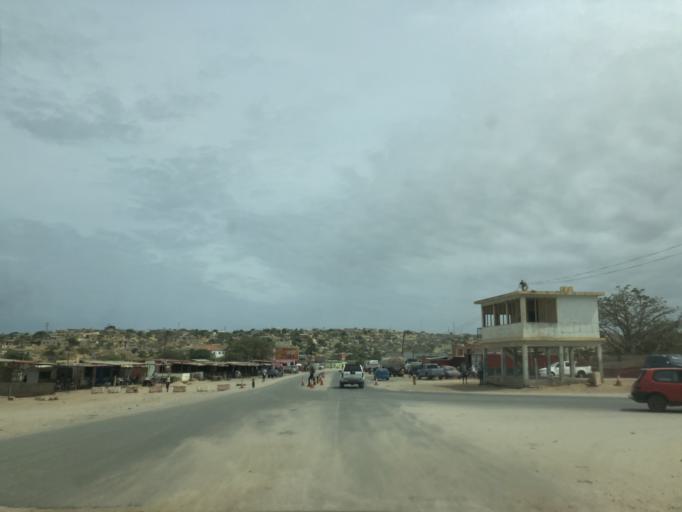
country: AO
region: Cuanza Sul
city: Sumbe
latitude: -11.2312
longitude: 13.8440
